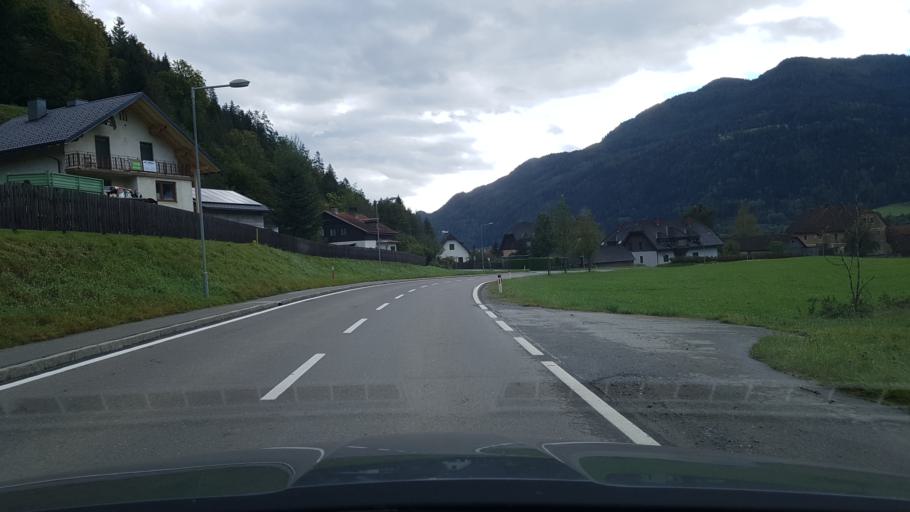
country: AT
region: Styria
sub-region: Politischer Bezirk Murau
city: Triebendorf
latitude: 47.1453
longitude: 14.2825
